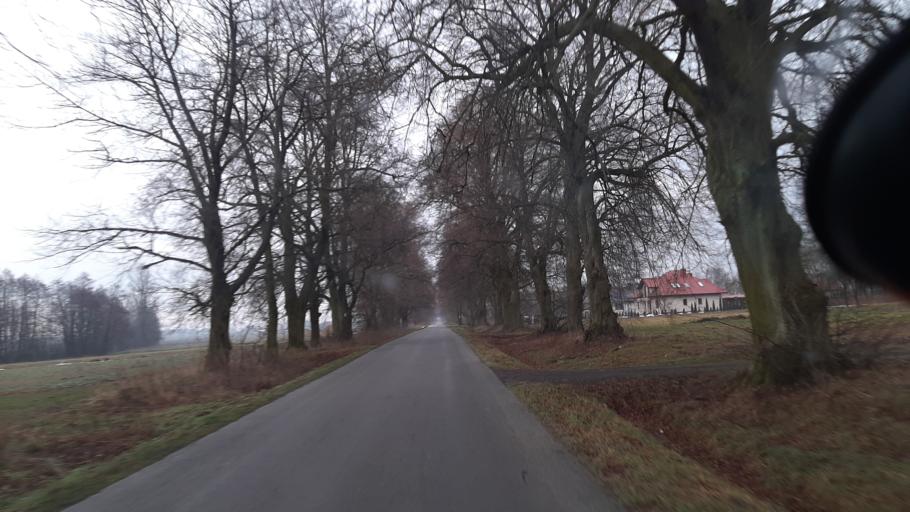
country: PL
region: Lublin Voivodeship
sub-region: Powiat lubelski
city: Jastkow
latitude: 51.3454
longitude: 22.5246
